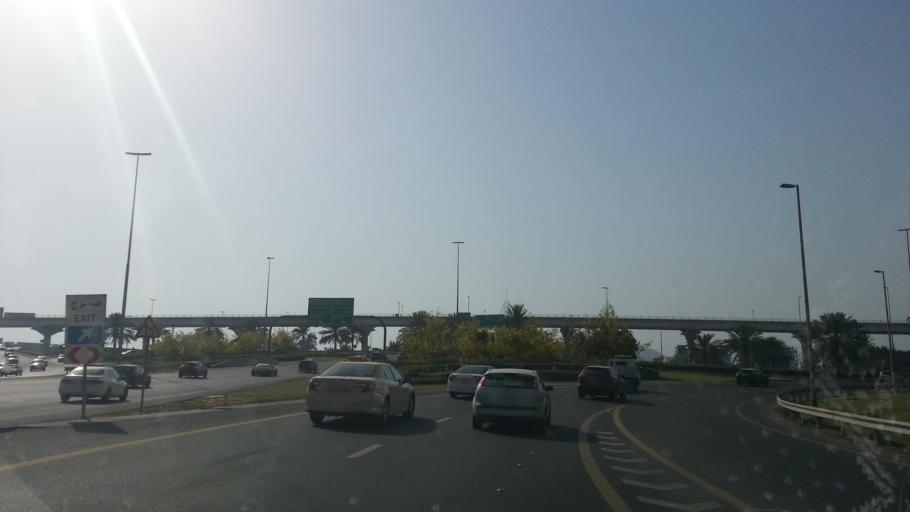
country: AE
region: Dubai
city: Dubai
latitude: 25.1215
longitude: 55.2046
